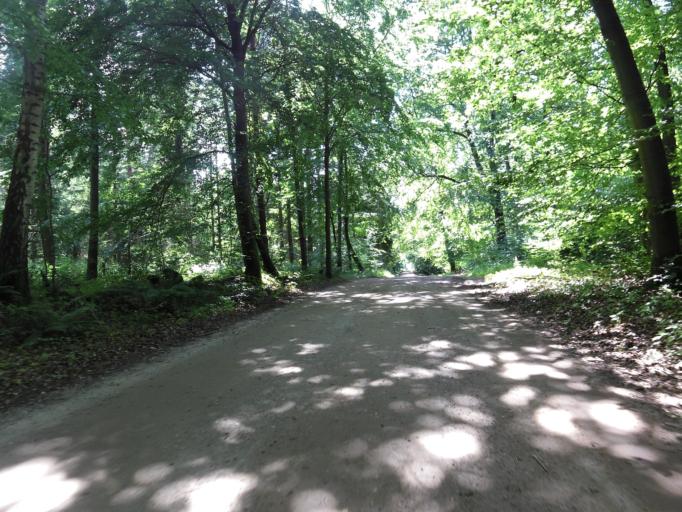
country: DE
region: Brandenburg
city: Lychen
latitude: 53.3000
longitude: 13.3718
